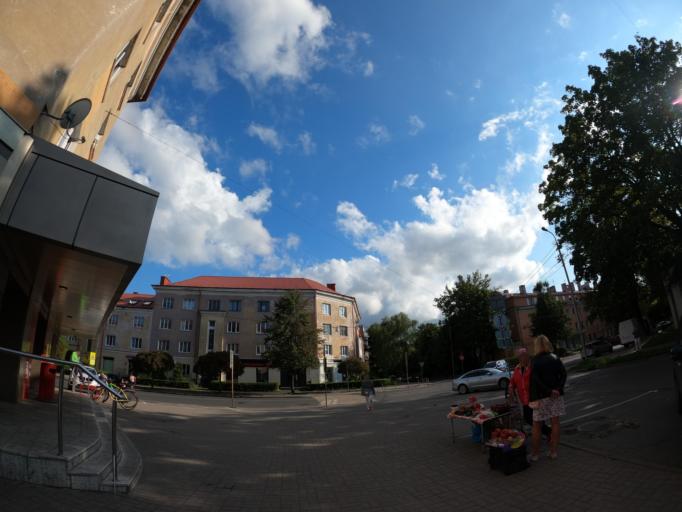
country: RU
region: Kaliningrad
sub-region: Gorod Kaliningrad
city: Kaliningrad
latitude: 54.7245
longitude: 20.4644
